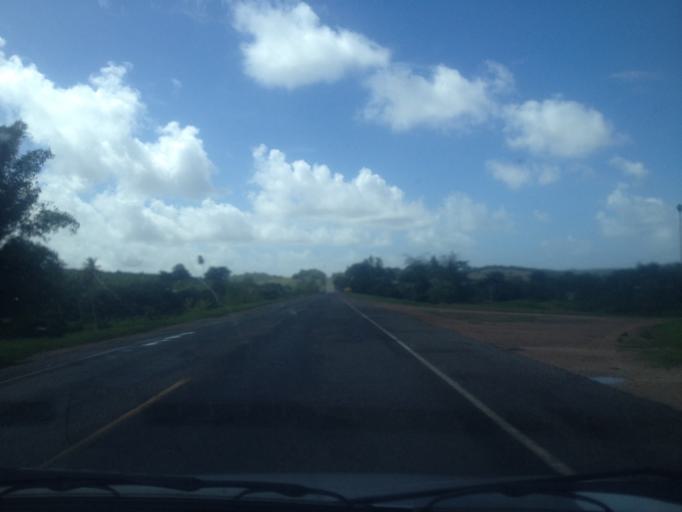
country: BR
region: Bahia
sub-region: Conde
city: Conde
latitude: -12.0558
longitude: -37.7195
